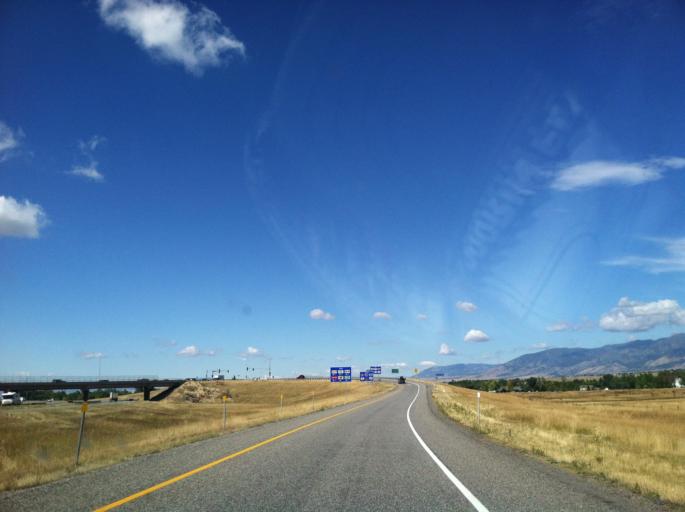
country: US
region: Montana
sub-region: Gallatin County
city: Bozeman
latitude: 45.7096
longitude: -111.0613
